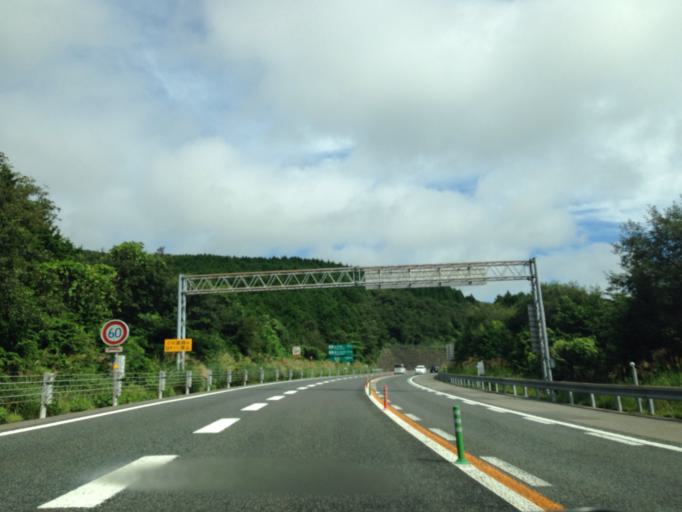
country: JP
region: Shizuoka
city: Gotemba
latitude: 35.3653
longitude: 138.8482
